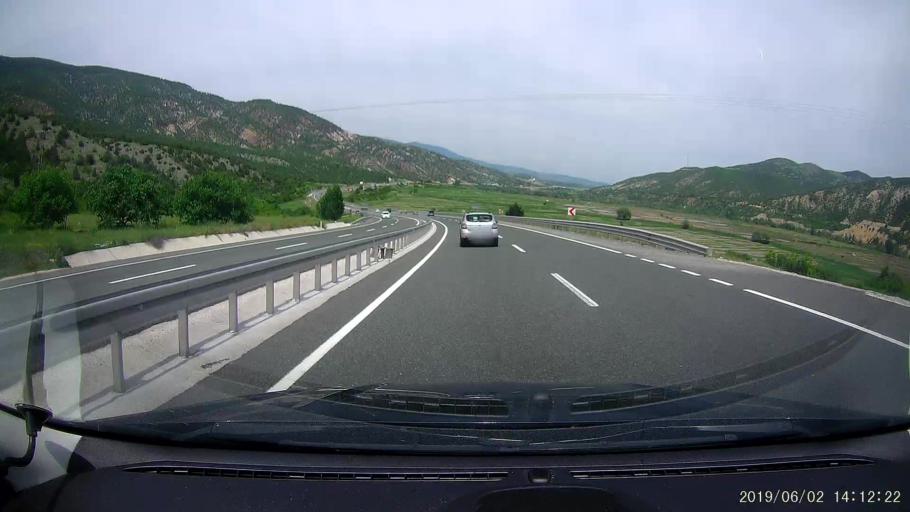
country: TR
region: Cankiri
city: Yaprakli
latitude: 40.9121
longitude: 33.8089
